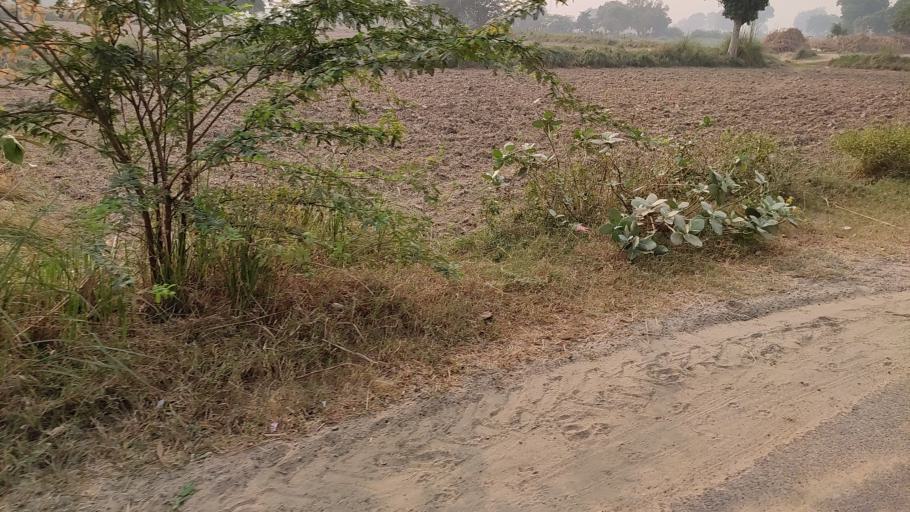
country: IN
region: Uttar Pradesh
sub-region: Mathura
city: Vrindavan
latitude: 27.5462
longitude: 77.7115
